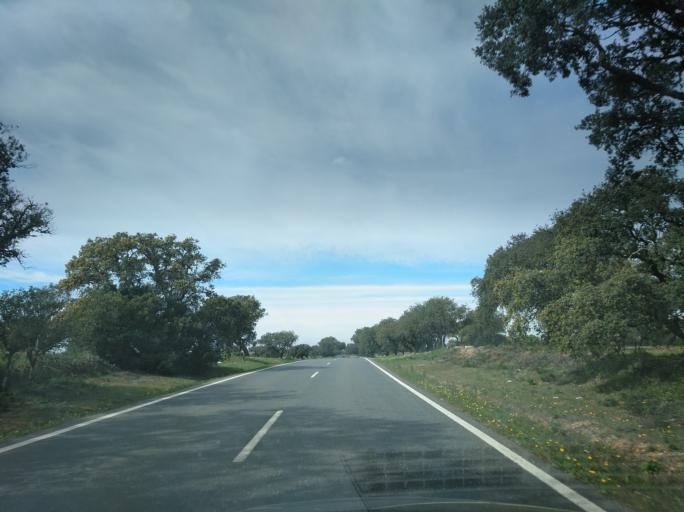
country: PT
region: Beja
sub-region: Mertola
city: Mertola
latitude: 37.7516
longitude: -7.8047
